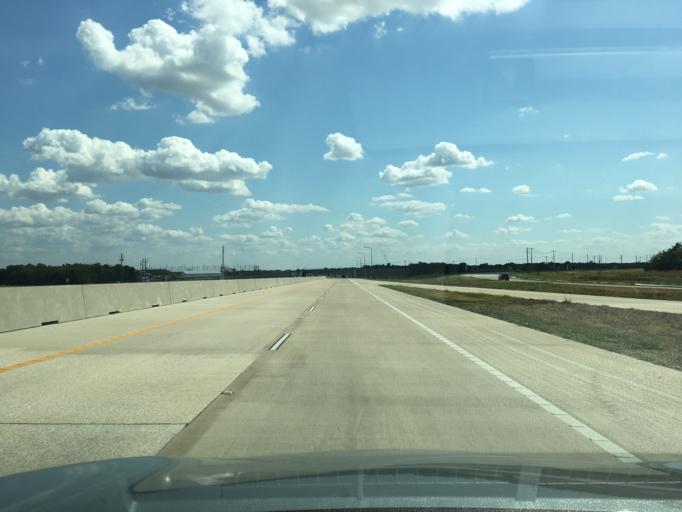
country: US
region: Texas
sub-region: Tarrant County
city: Mansfield
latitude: 32.5666
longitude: -97.0837
